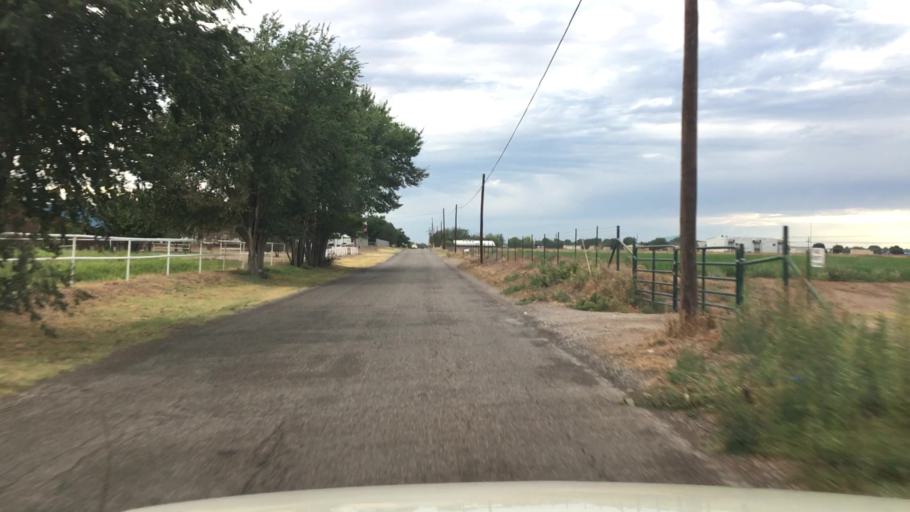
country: US
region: New Mexico
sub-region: Chaves County
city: Roswell
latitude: 33.4160
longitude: -104.4997
